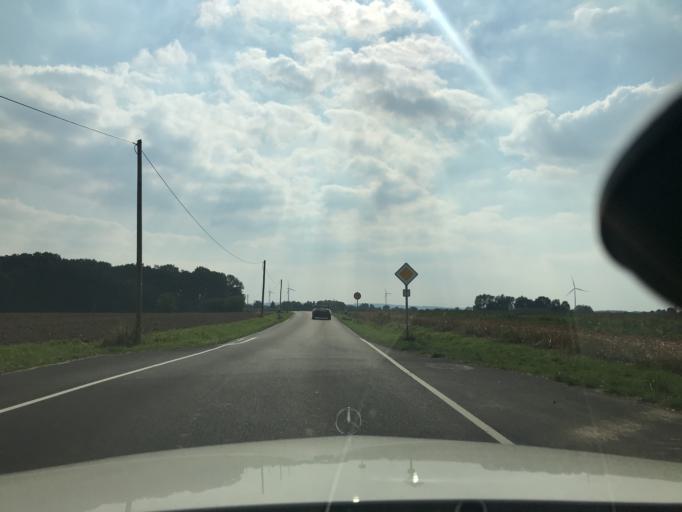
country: DE
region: North Rhine-Westphalia
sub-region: Regierungsbezirk Arnsberg
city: Werl
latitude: 51.5878
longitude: 7.8705
